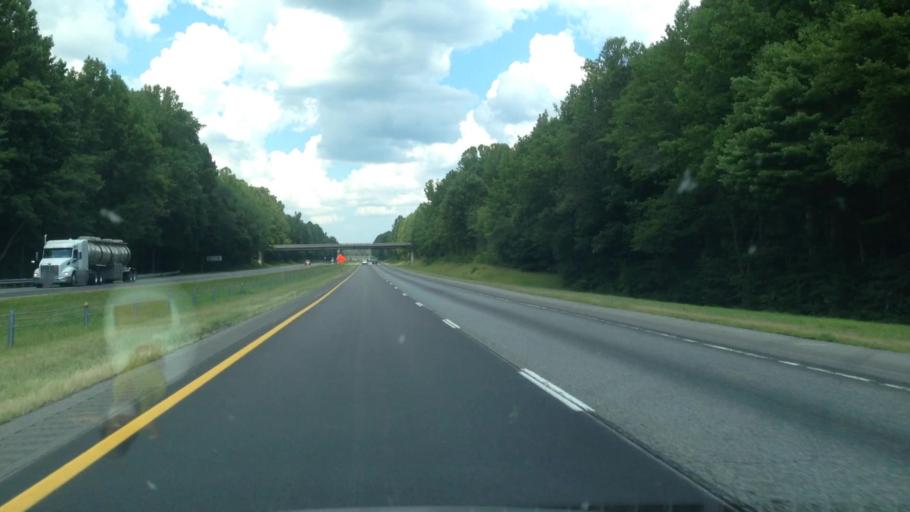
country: US
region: North Carolina
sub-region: Rockingham County
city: Reidsville
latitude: 36.4488
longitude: -79.5597
